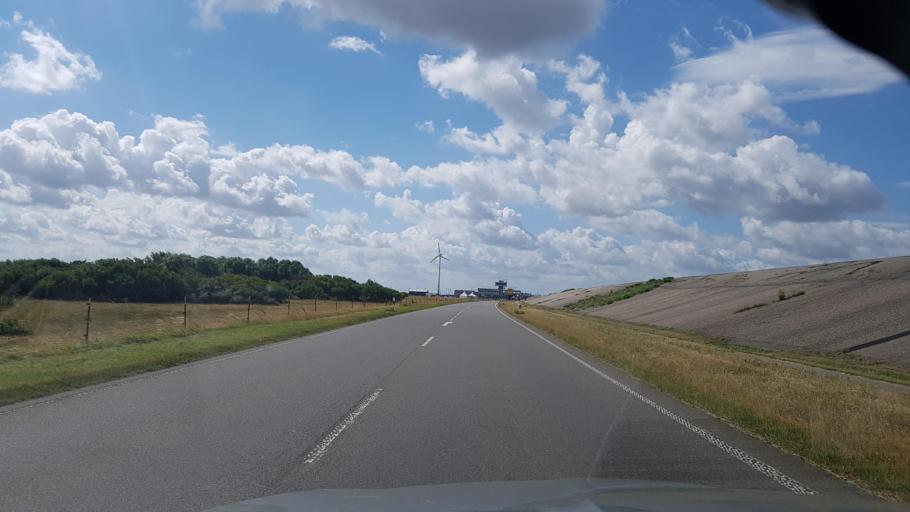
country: DE
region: Schleswig-Holstein
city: Wesselburenerkoog
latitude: 54.2718
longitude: 8.8454
